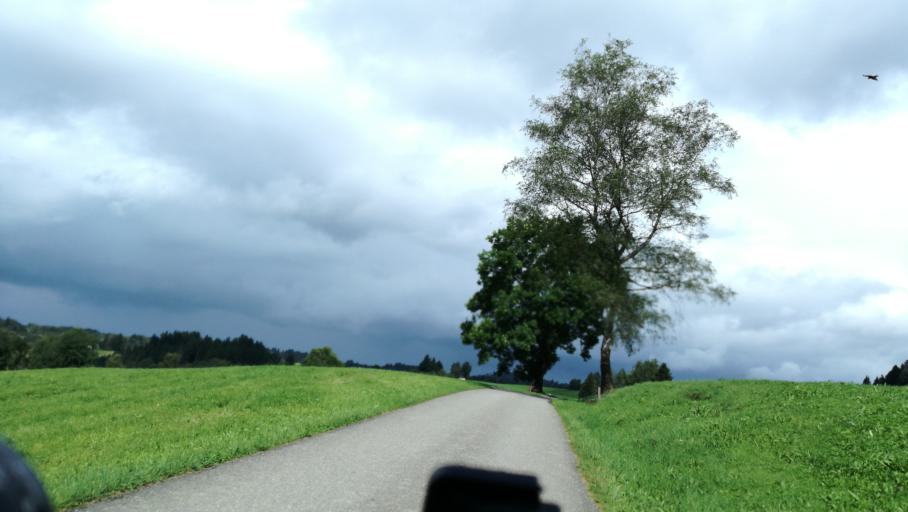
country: CH
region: Zug
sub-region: Zug
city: Walchwil
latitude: 47.1053
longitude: 8.5463
